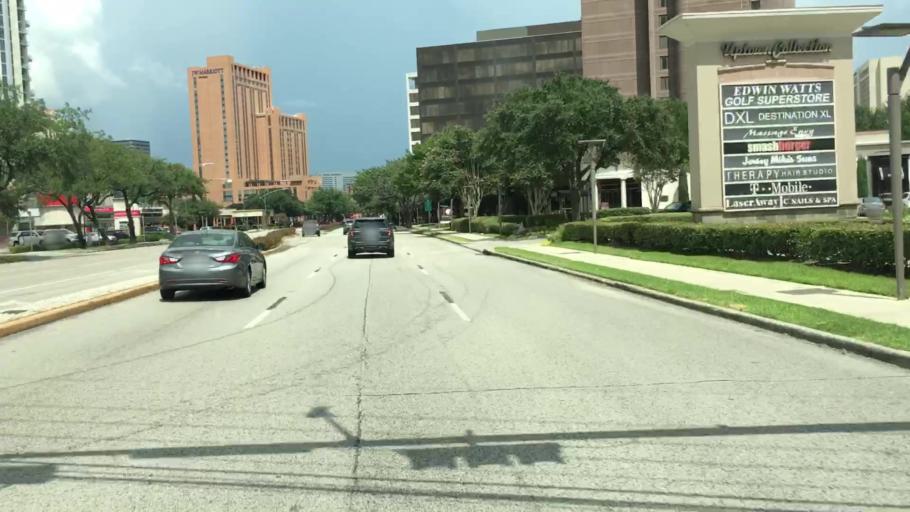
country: US
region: Texas
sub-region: Harris County
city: Bellaire
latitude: 29.7392
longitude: -95.4705
